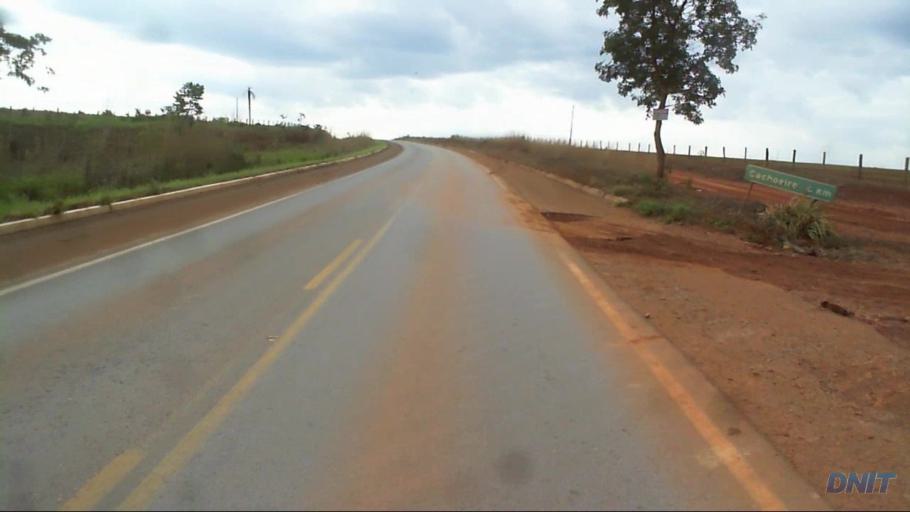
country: BR
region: Goias
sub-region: Uruacu
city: Uruacu
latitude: -14.6891
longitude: -49.1287
